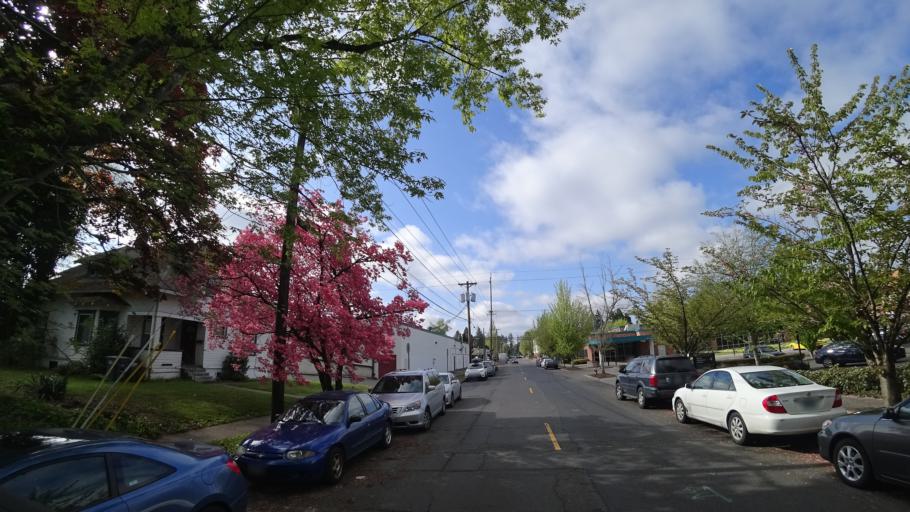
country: US
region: Oregon
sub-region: Washington County
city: Hillsboro
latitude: 45.5208
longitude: -122.9755
